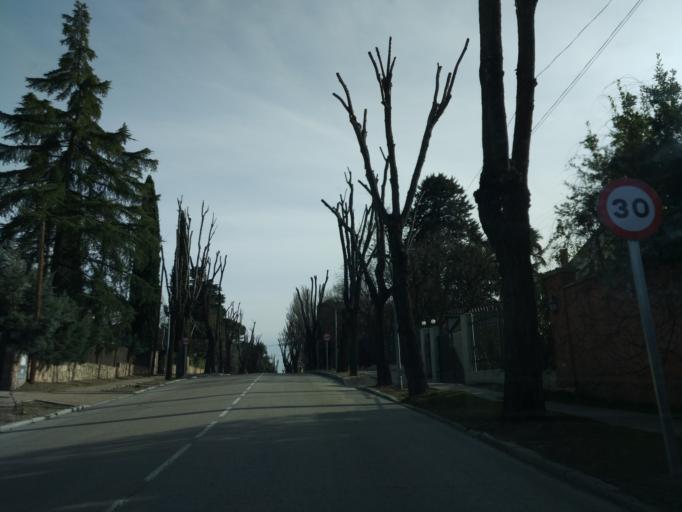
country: ES
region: Madrid
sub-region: Provincia de Madrid
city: Tetuan de las Victorias
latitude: 40.4662
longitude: -3.7314
